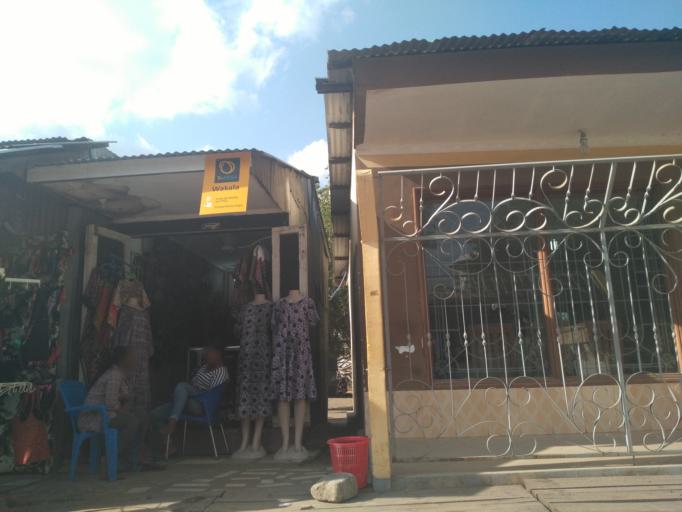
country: TZ
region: Dar es Salaam
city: Dar es Salaam
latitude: -6.8219
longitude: 39.3028
